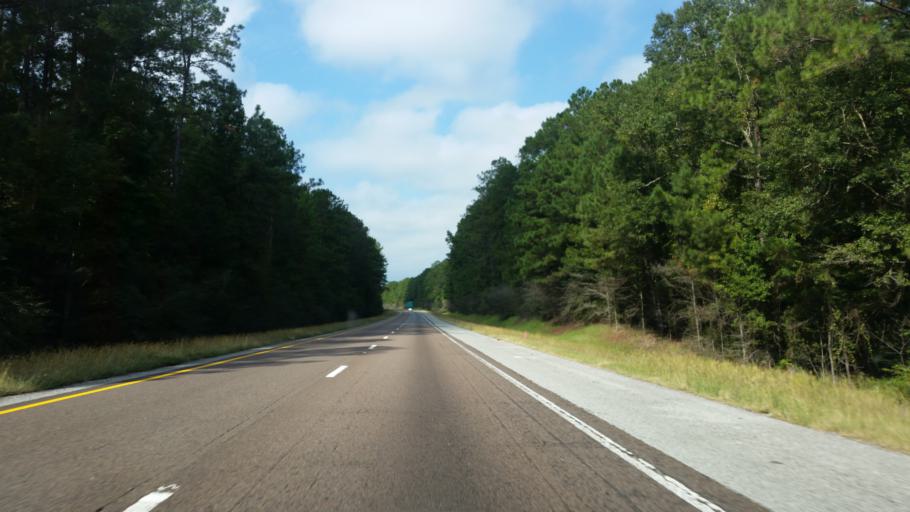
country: US
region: Alabama
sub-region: Baldwin County
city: Bay Minette
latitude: 30.9586
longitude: -87.7973
